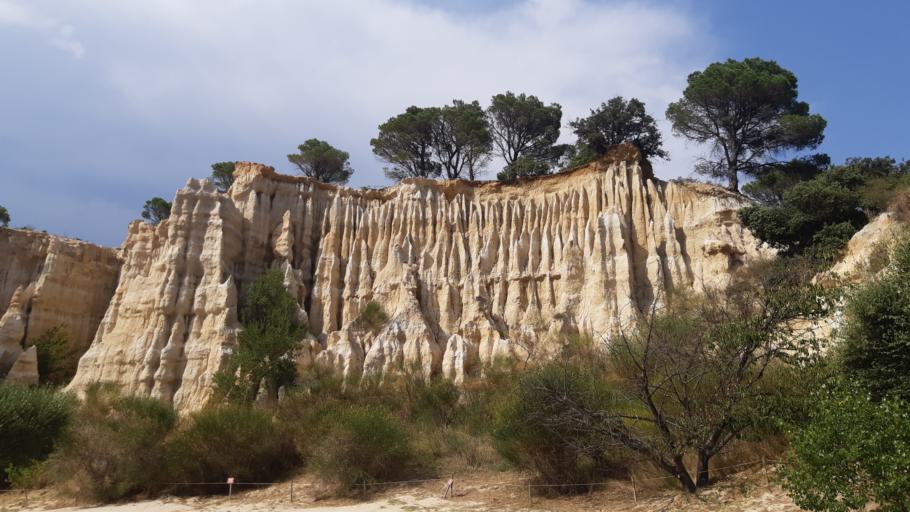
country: FR
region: Languedoc-Roussillon
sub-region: Departement des Pyrenees-Orientales
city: Ille-sur-Tet
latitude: 42.6859
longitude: 2.6219
